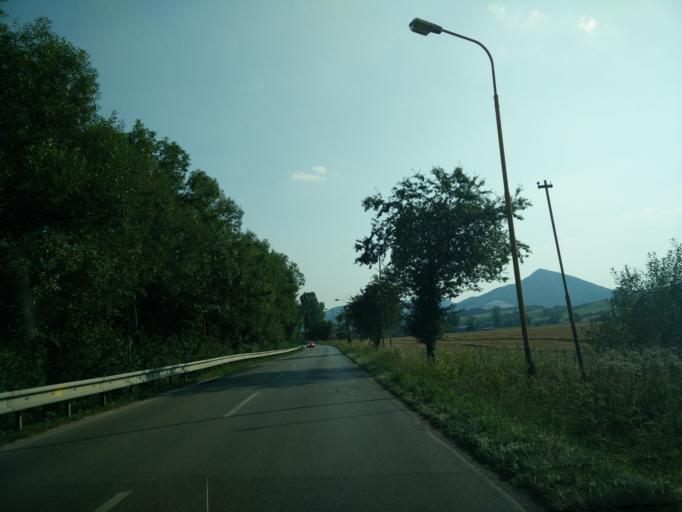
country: SK
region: Zilinsky
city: Rajec
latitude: 49.0766
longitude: 18.6307
